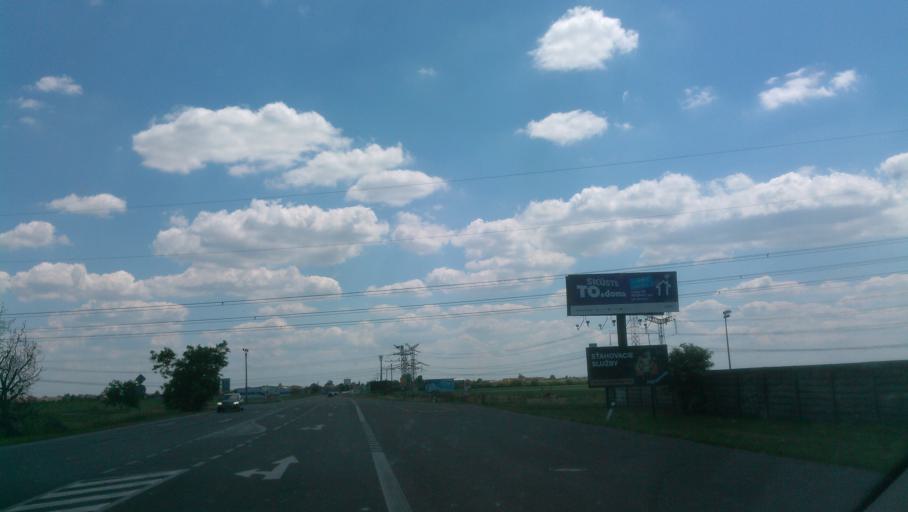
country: SK
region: Bratislavsky
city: Dunajska Luzna
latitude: 48.1122
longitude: 17.2206
